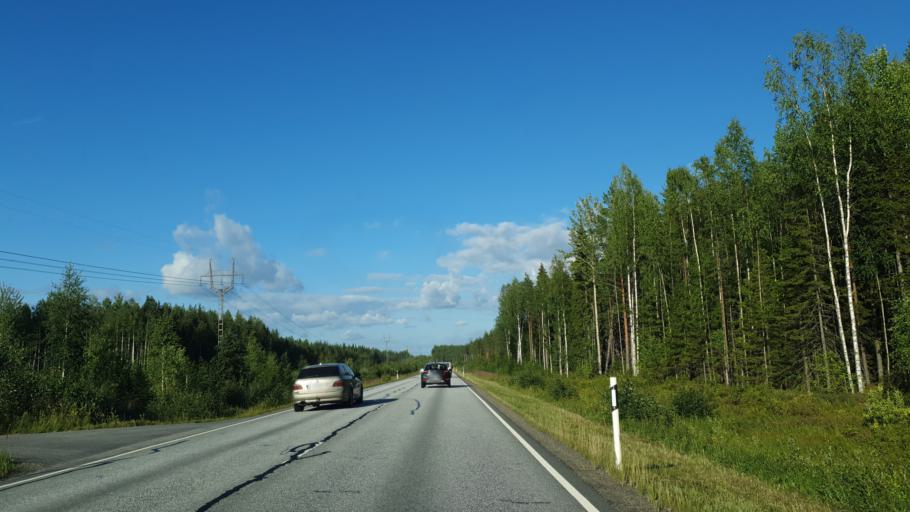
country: FI
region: North Karelia
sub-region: Joensuu
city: Outokumpu
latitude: 62.5332
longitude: 29.0978
